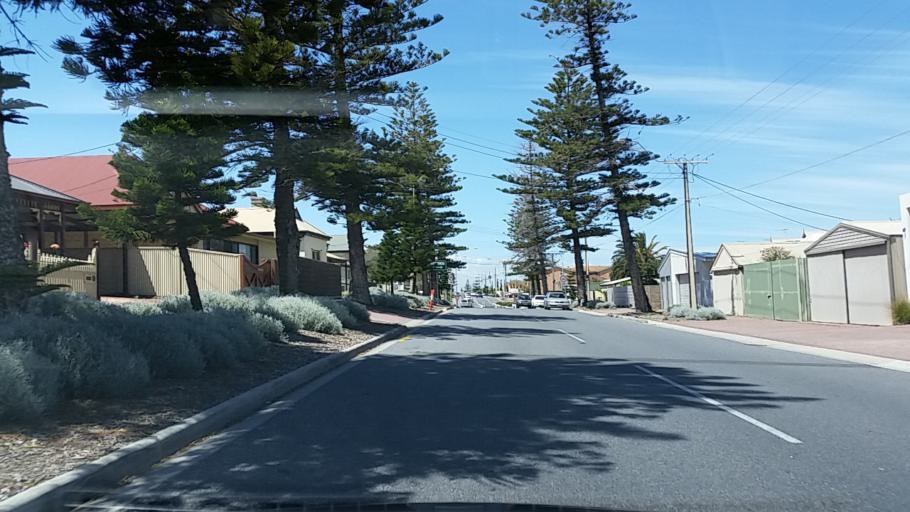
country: AU
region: South Australia
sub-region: Charles Sturt
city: Grange
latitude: -34.9062
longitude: 138.4908
